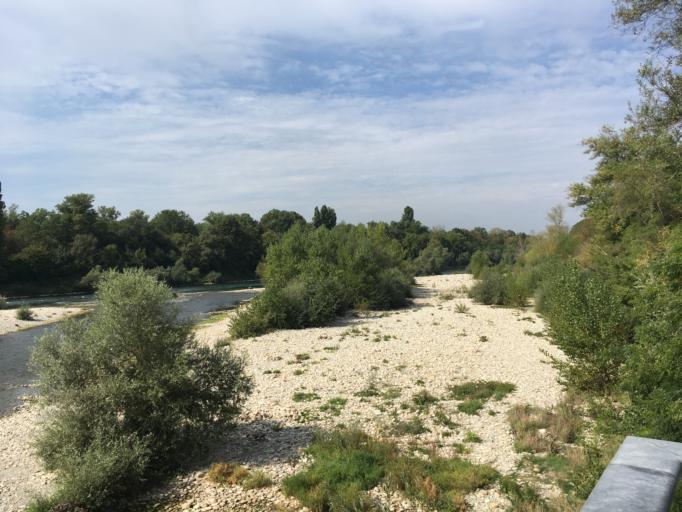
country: FR
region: Alsace
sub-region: Departement du Haut-Rhin
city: Rosenau
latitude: 47.6474
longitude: 7.5425
